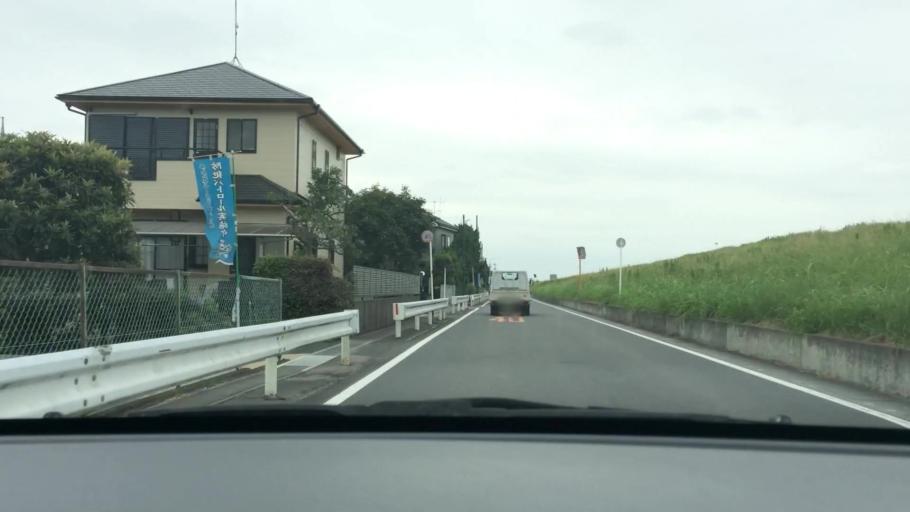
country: JP
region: Chiba
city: Matsudo
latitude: 35.7861
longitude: 139.8886
